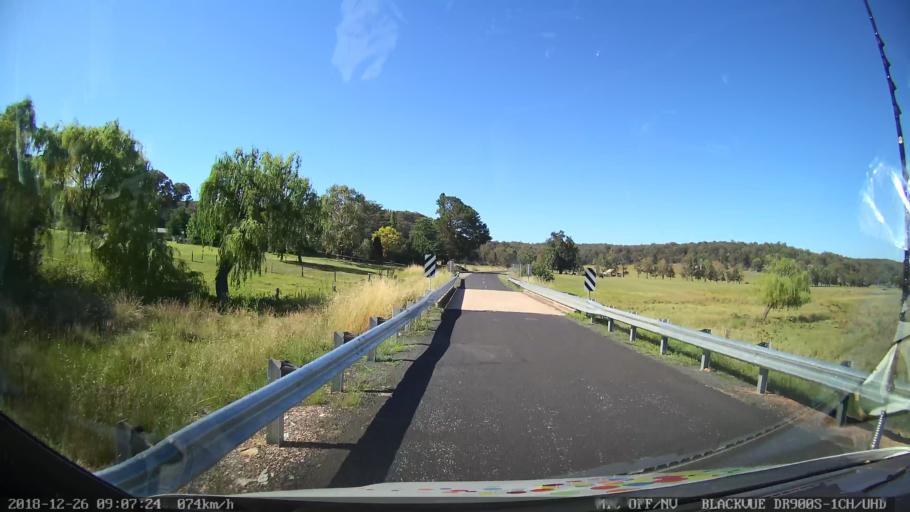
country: AU
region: New South Wales
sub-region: Mid-Western Regional
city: Kandos
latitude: -32.7051
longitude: 150.0044
